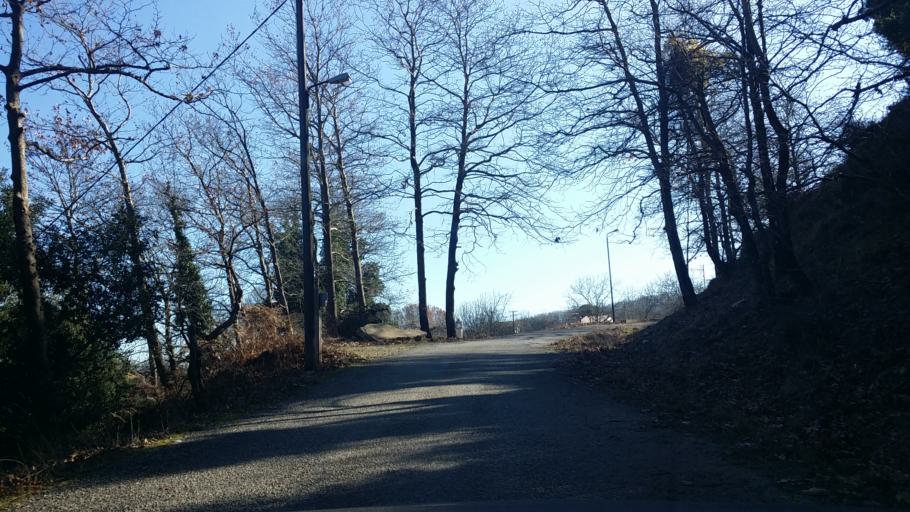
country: GR
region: West Greece
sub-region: Nomos Aitolias kai Akarnanias
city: Krikellos
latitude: 39.0071
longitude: 21.2707
